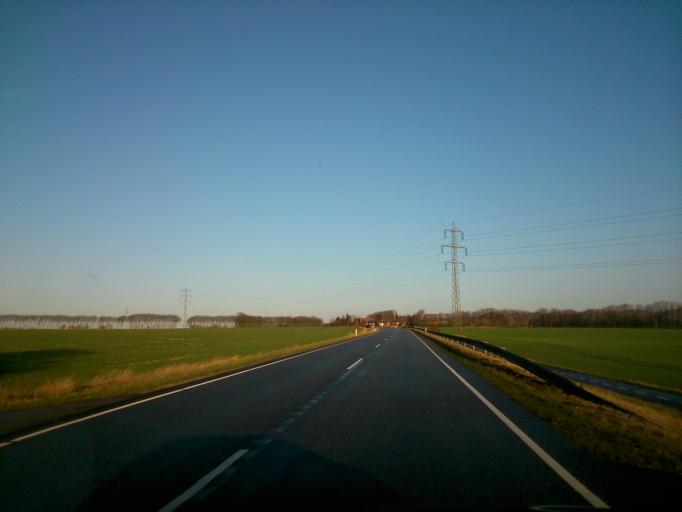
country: DK
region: Central Jutland
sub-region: Ringkobing-Skjern Kommune
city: Tarm
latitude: 55.9802
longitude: 8.5889
